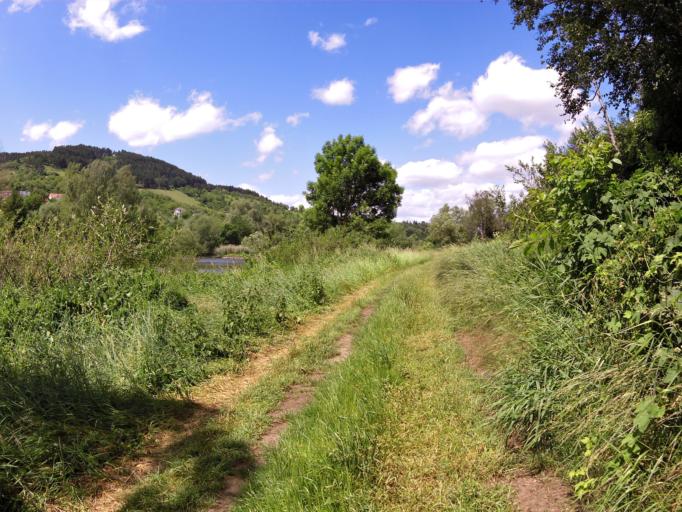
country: DE
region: Bavaria
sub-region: Regierungsbezirk Unterfranken
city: Erlabrunn
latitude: 49.8619
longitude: 9.8451
